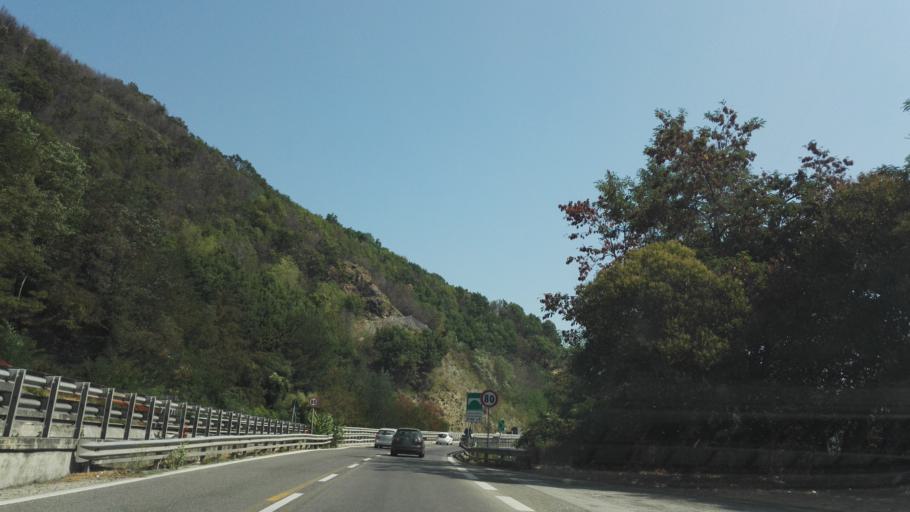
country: IT
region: Calabria
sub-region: Provincia di Cosenza
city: Altilia
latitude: 39.1288
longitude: 16.2661
